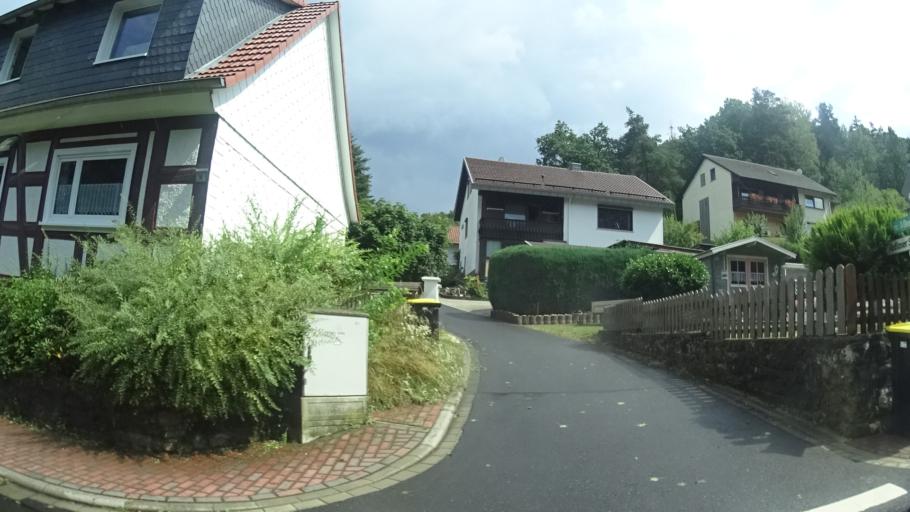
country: DE
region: Hesse
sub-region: Regierungsbezirk Giessen
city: Lauterbach
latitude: 50.6214
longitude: 9.4392
